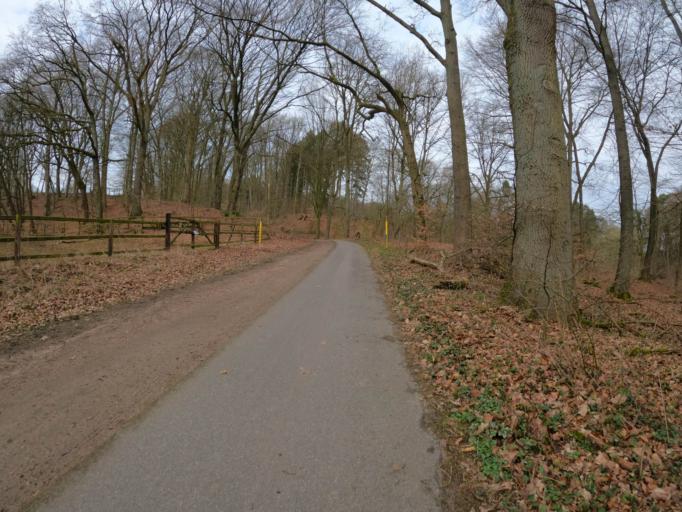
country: DE
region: Lower Saxony
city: Seevetal
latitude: 53.4462
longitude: 9.9120
